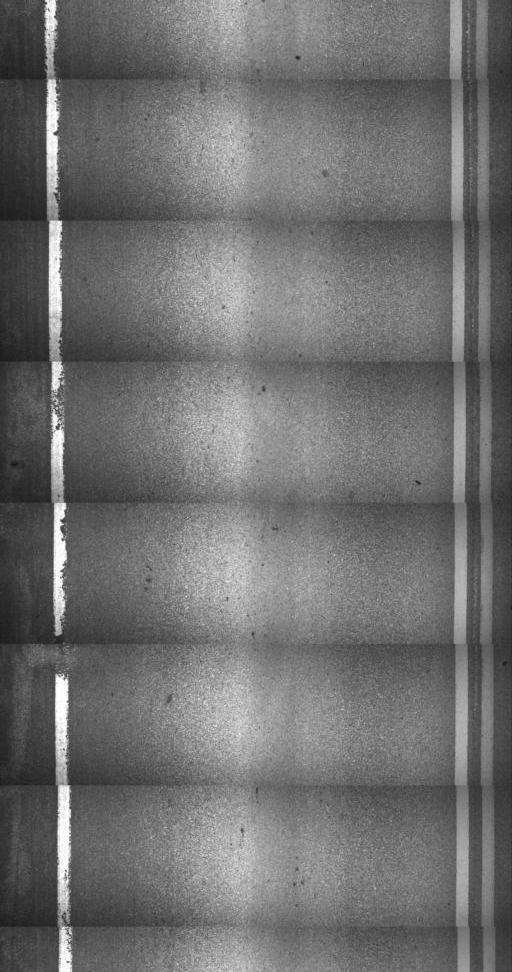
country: US
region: Vermont
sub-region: Franklin County
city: Enosburg Falls
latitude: 44.9127
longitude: -72.9564
